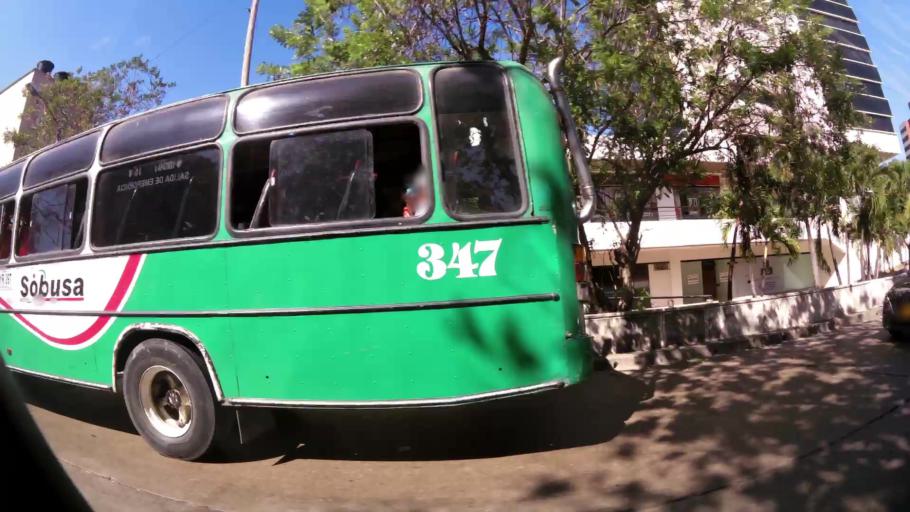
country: CO
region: Atlantico
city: Barranquilla
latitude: 11.0034
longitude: -74.8057
